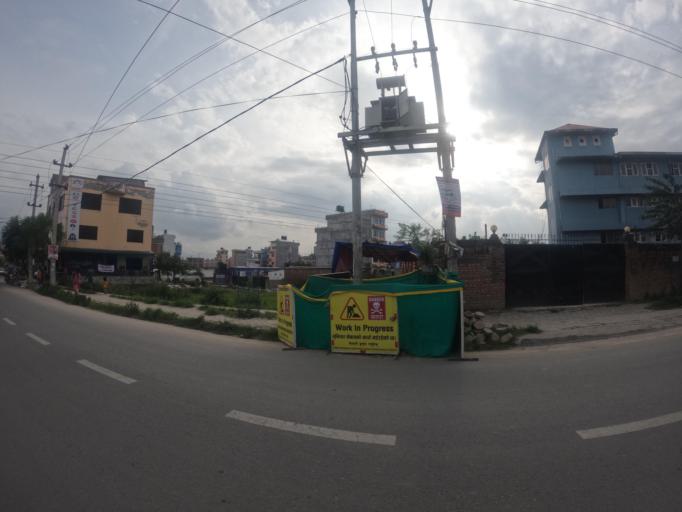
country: NP
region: Central Region
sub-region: Bagmati Zone
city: Bhaktapur
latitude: 27.6797
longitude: 85.3986
